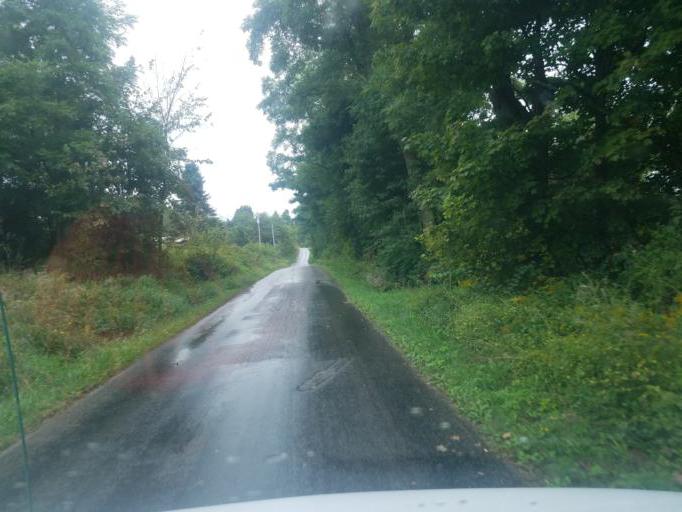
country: US
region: Ohio
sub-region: Wayne County
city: West Salem
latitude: 40.9190
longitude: -82.1531
